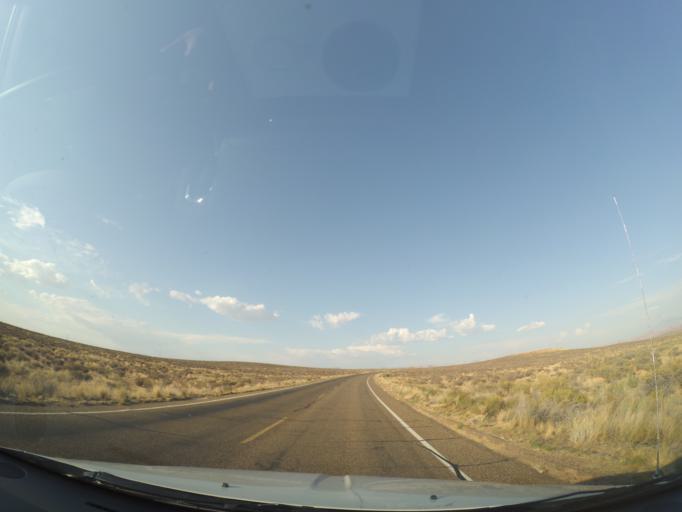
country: US
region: Arizona
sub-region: Coconino County
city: Page
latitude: 36.9831
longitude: -111.5256
